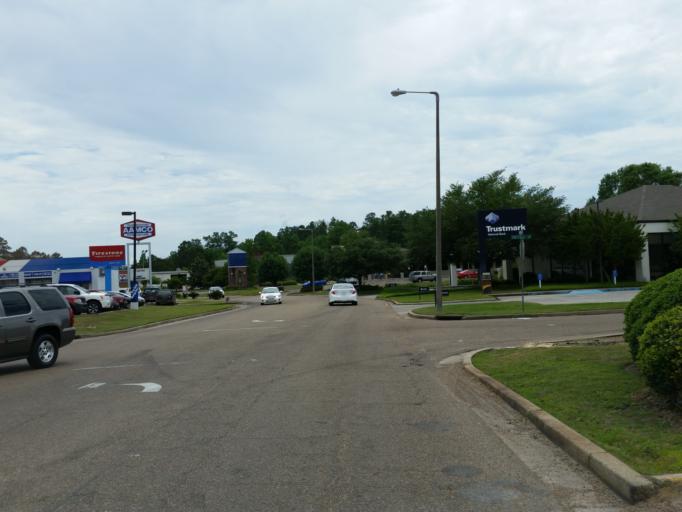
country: US
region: Mississippi
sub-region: Lamar County
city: West Hattiesburg
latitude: 31.3227
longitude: -89.3636
